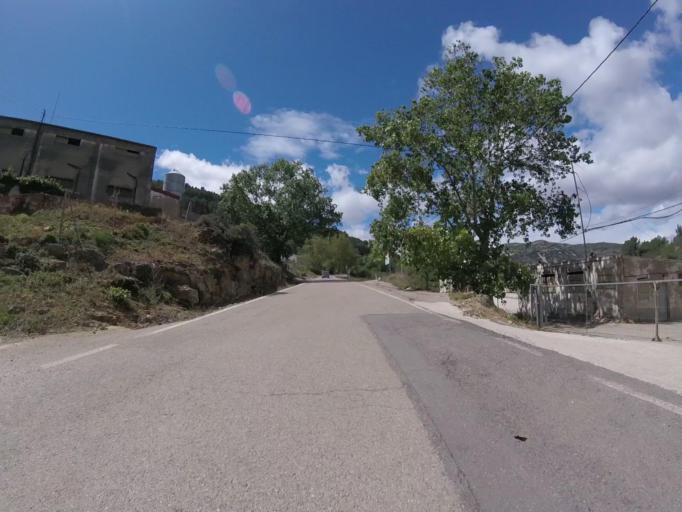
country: ES
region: Valencia
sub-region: Provincia de Castello
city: Sierra-Engarceran
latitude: 40.2718
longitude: -0.0122
